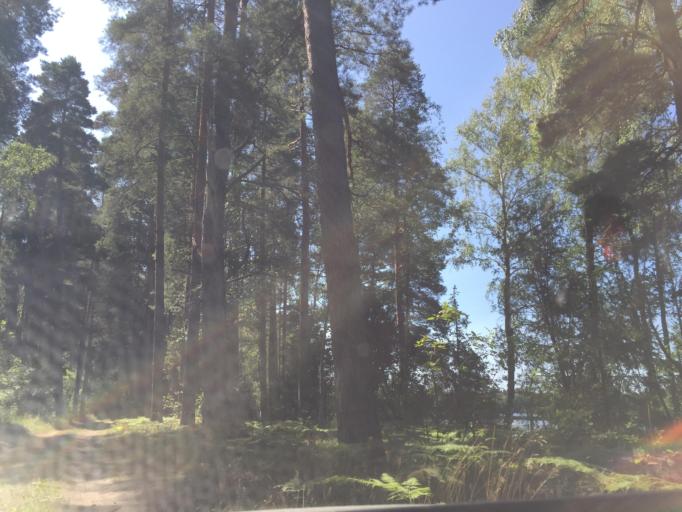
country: LV
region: Talsu Rajons
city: Stende
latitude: 57.1601
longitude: 22.3039
